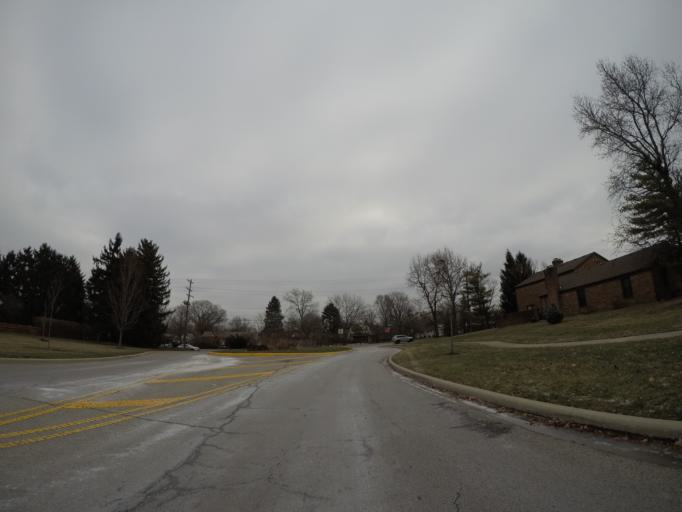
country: US
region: Ohio
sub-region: Franklin County
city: Upper Arlington
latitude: 40.0468
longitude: -83.0508
